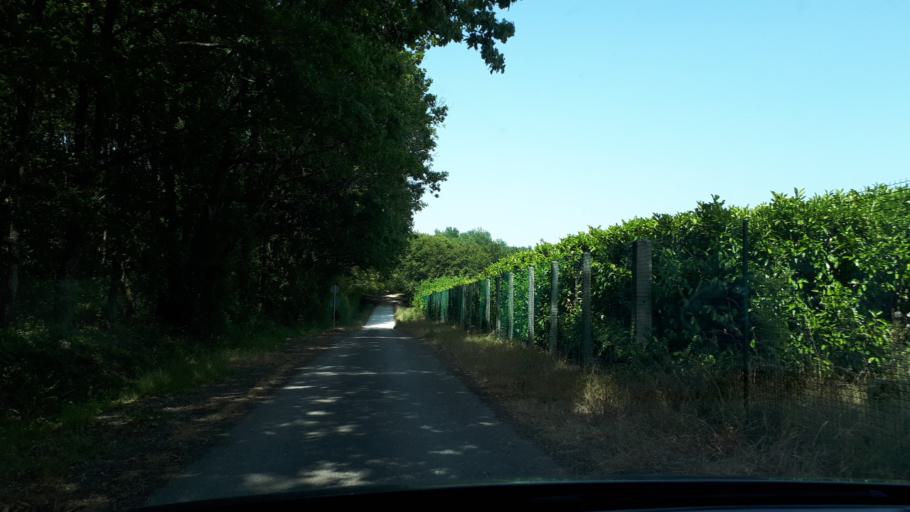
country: FR
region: Centre
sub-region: Departement du Loir-et-Cher
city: Vendome
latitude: 47.8254
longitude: 1.0537
